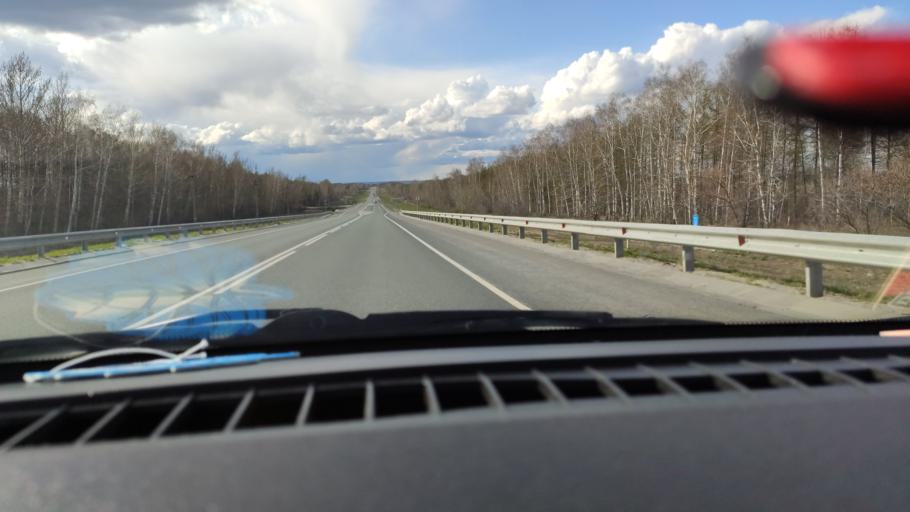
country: RU
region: Saratov
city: Shikhany
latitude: 52.1518
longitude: 47.1868
